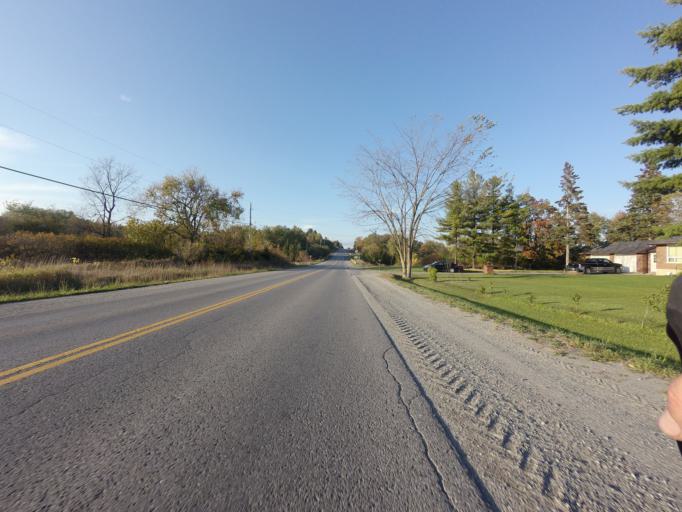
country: CA
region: Ontario
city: Kingston
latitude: 44.3683
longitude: -76.4243
